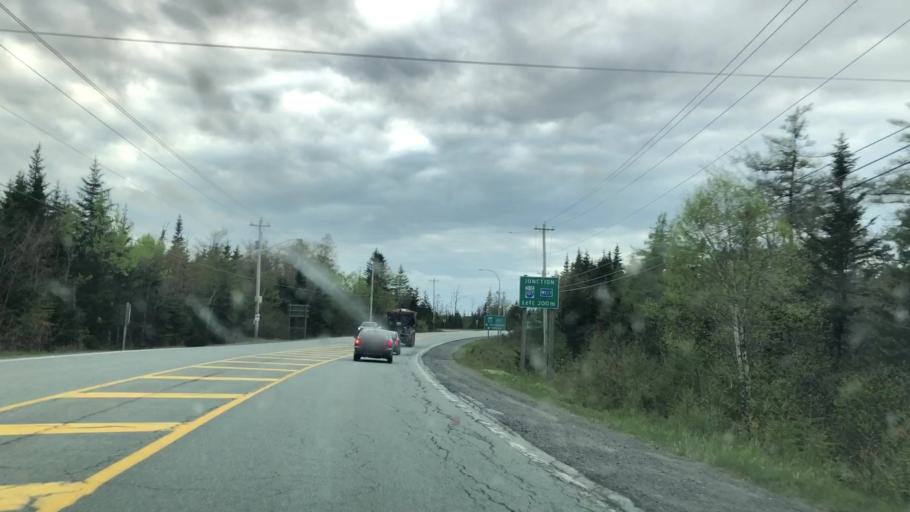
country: CA
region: Nova Scotia
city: Cole Harbour
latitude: 44.7819
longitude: -63.1747
